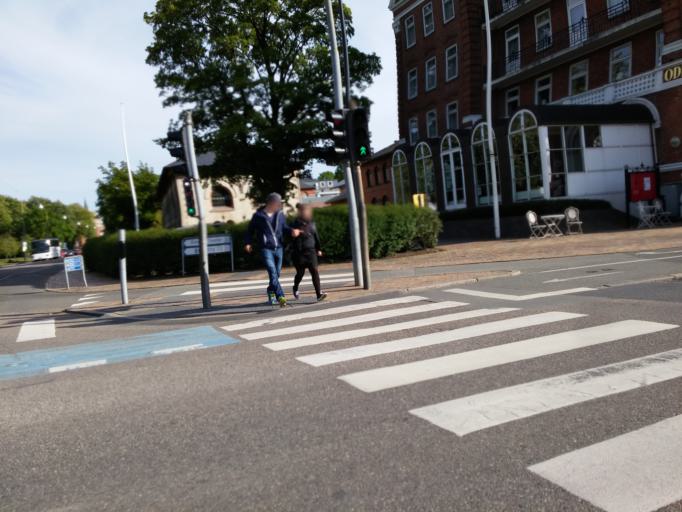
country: DK
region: South Denmark
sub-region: Odense Kommune
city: Odense
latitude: 55.4004
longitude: 10.3831
